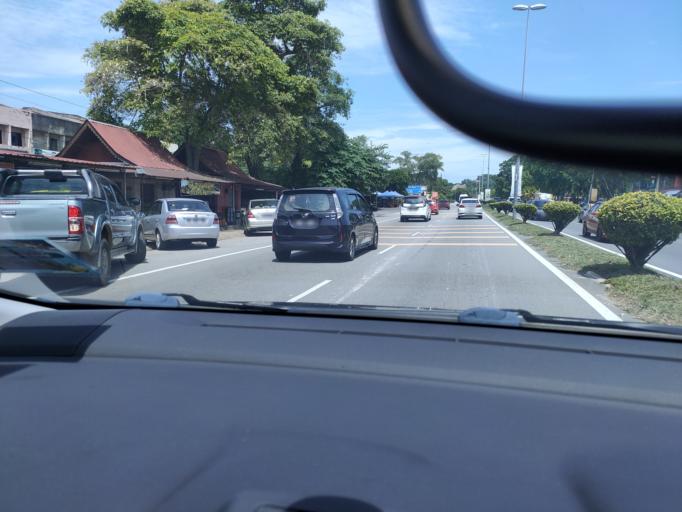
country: MY
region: Melaka
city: Bukit Rambai
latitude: 2.2688
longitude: 102.2172
